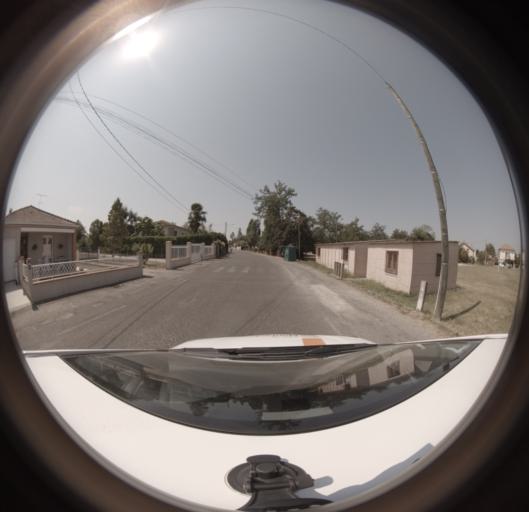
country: FR
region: Midi-Pyrenees
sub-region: Departement du Tarn-et-Garonne
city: Montauban
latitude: 44.0205
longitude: 1.3698
